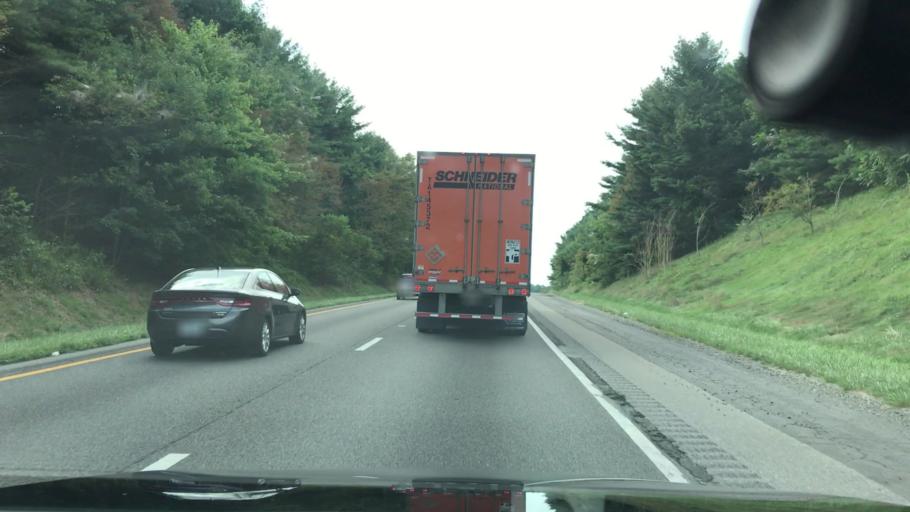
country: US
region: Virginia
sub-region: Carroll County
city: Woodlawn
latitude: 36.7614
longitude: -80.7940
